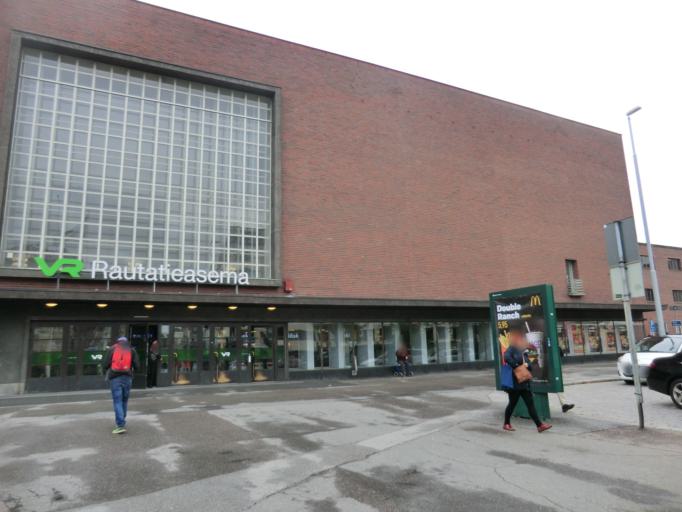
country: FI
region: Pirkanmaa
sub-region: Tampere
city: Tampere
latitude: 61.4986
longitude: 23.7725
